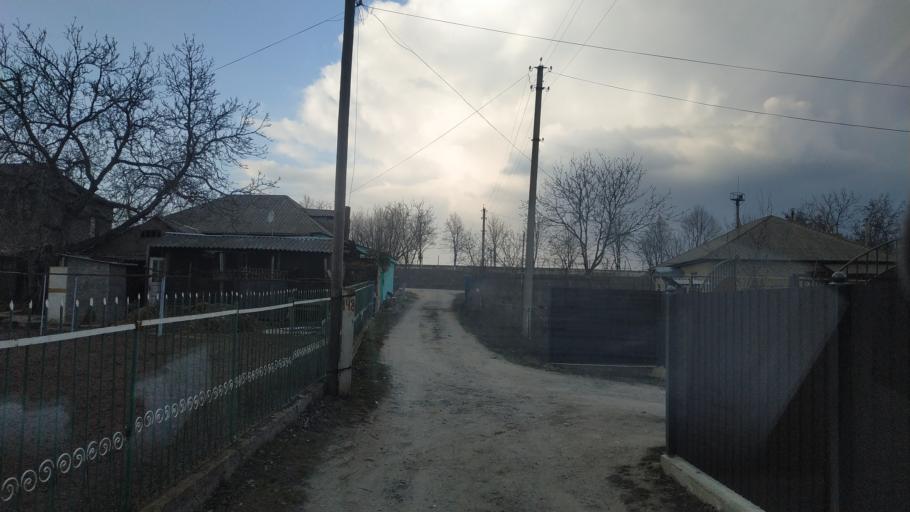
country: MD
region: Telenesti
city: Grigoriopol
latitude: 47.0086
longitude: 29.3046
